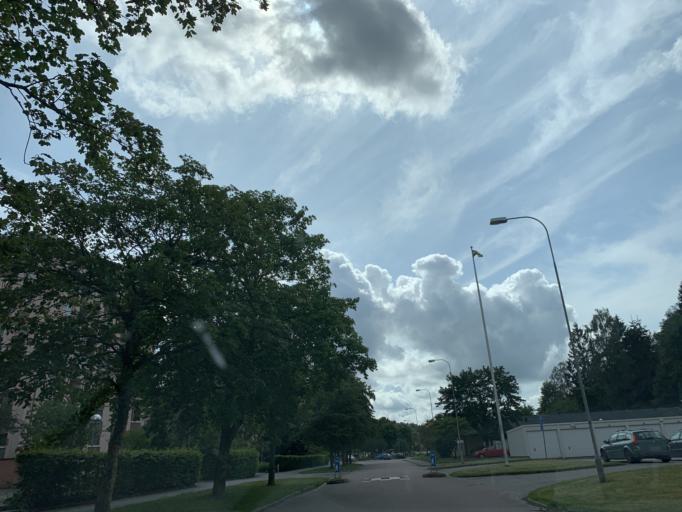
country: SE
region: Vaestra Goetaland
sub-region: Goteborg
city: Eriksbo
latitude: 57.7622
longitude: 12.0606
